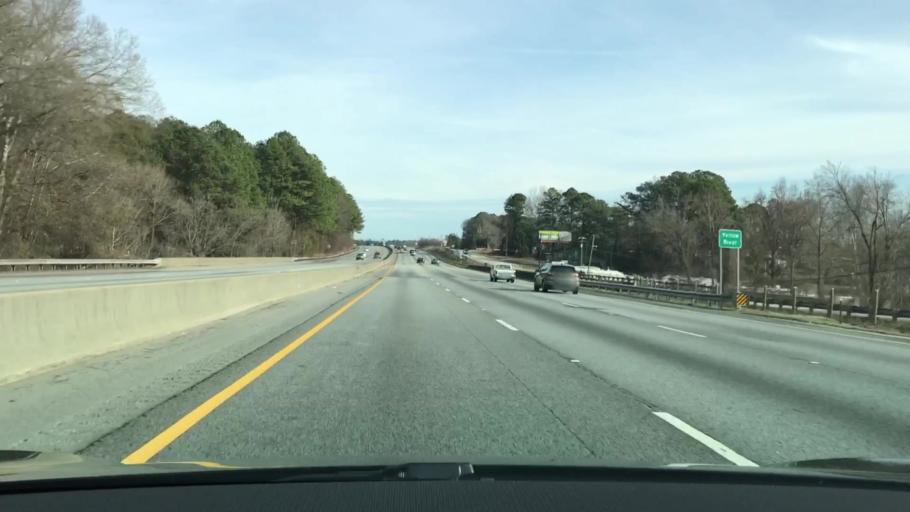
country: US
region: Georgia
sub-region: Newton County
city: Porterdale
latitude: 33.6149
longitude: -83.9161
